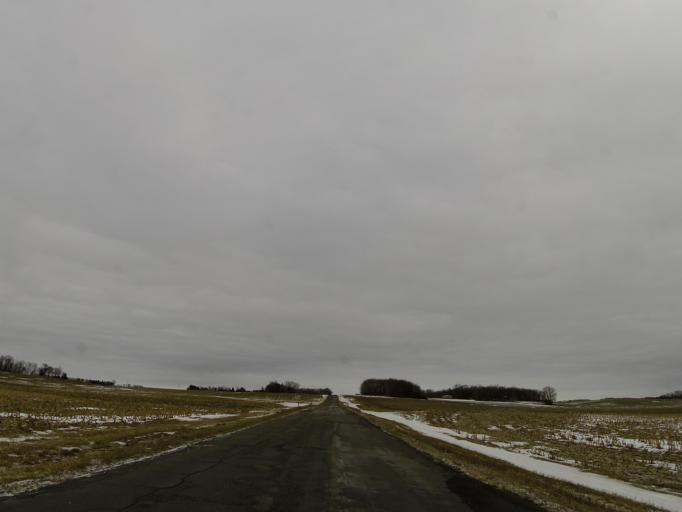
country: US
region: Minnesota
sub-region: Washington County
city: Cottage Grove
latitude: 44.8047
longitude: -92.8845
